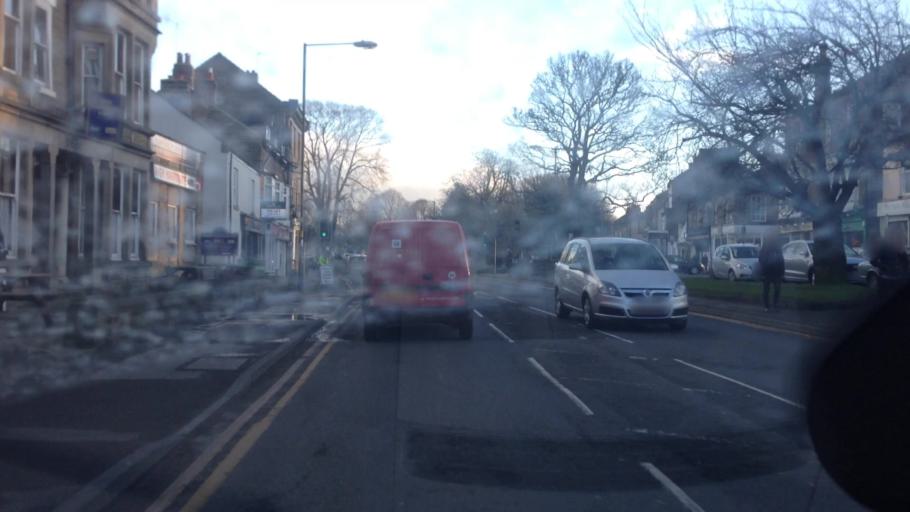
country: GB
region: England
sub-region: North Yorkshire
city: Harrogate
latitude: 53.9982
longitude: -1.5299
